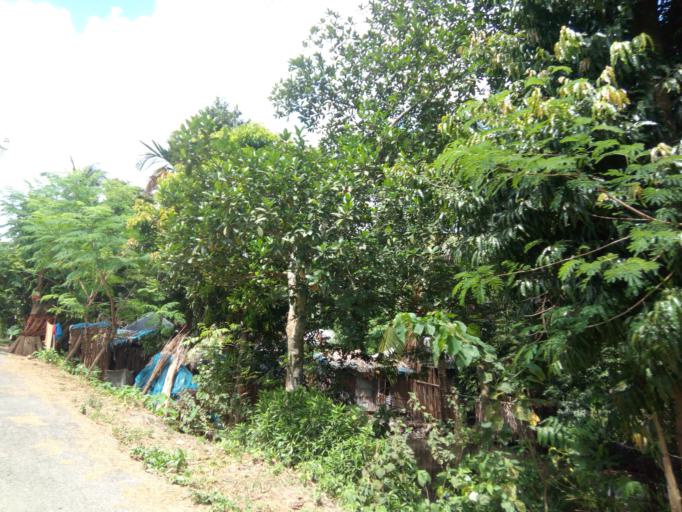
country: BD
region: Khulna
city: Kalia
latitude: 23.0148
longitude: 89.7189
